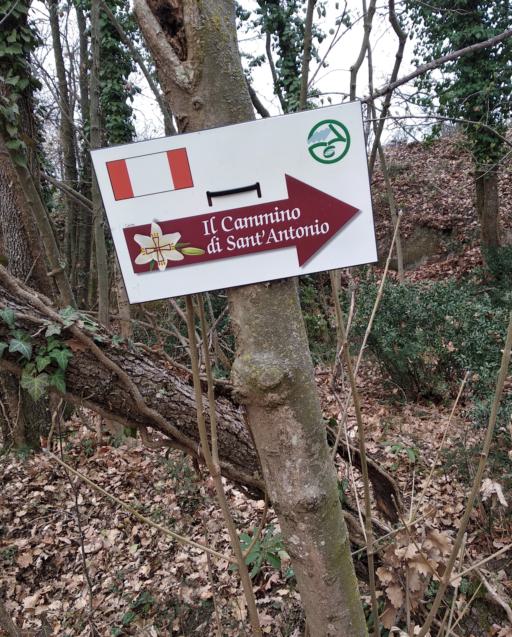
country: IT
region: Emilia-Romagna
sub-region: Provincia di Bologna
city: Pulce
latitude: 44.4290
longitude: 11.4071
